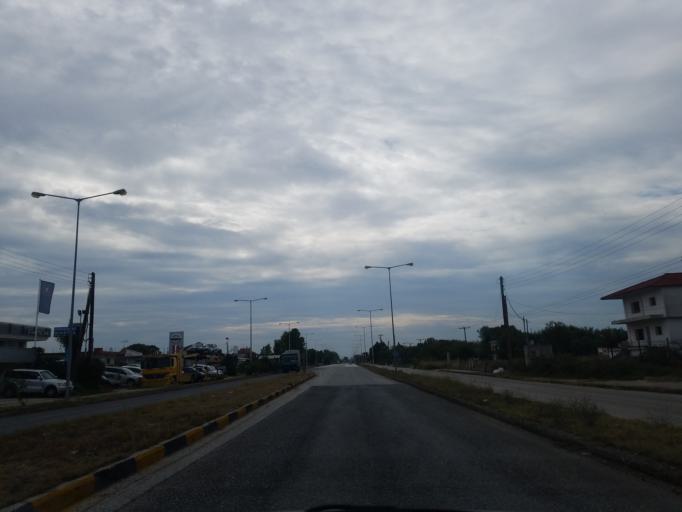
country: GR
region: Thessaly
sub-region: Trikala
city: Pyrgetos
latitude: 39.5845
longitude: 21.7393
